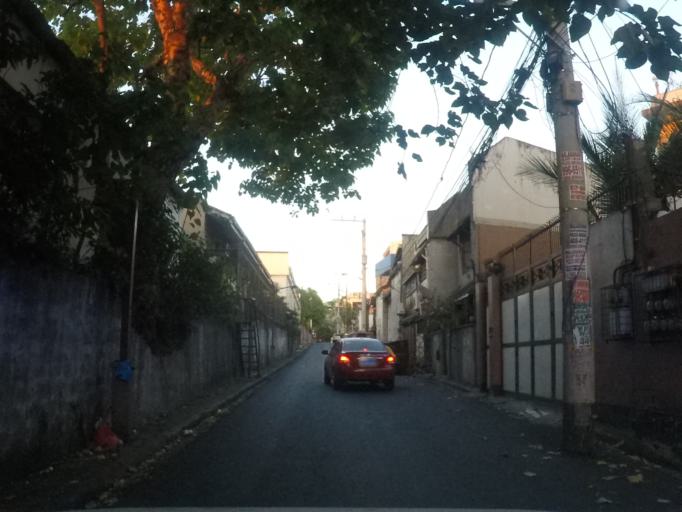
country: PH
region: Metro Manila
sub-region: San Juan
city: San Juan
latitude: 14.6035
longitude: 121.0266
